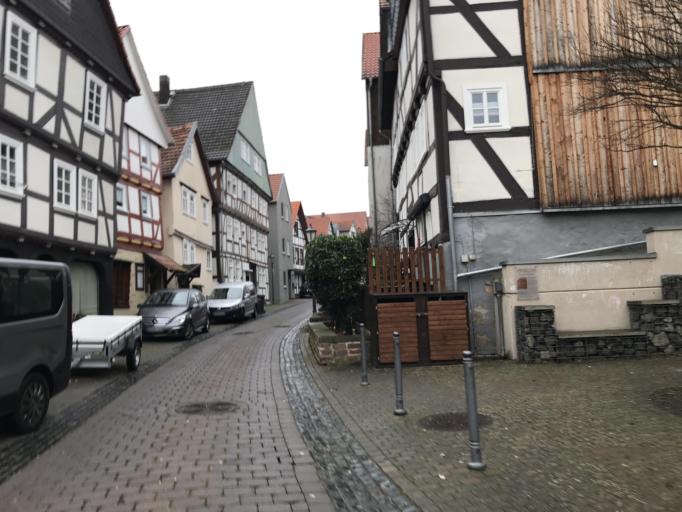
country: DE
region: Hesse
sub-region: Regierungsbezirk Kassel
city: Bad Wildungen
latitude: 51.1198
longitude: 9.1262
